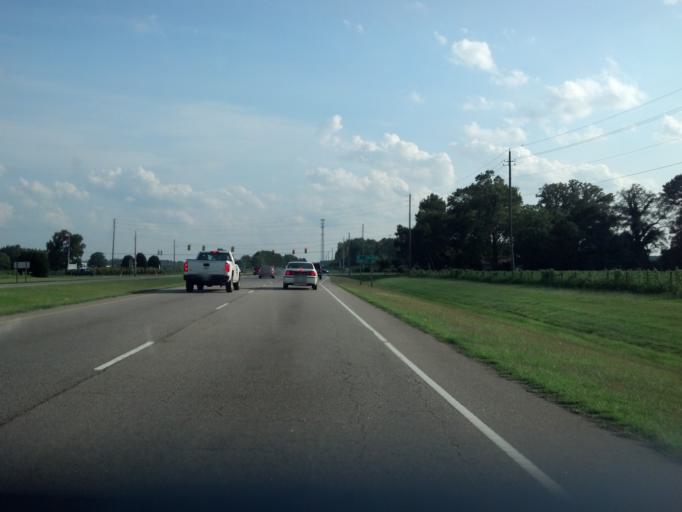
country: US
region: North Carolina
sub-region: Pitt County
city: Winterville
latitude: 35.5299
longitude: -77.4080
